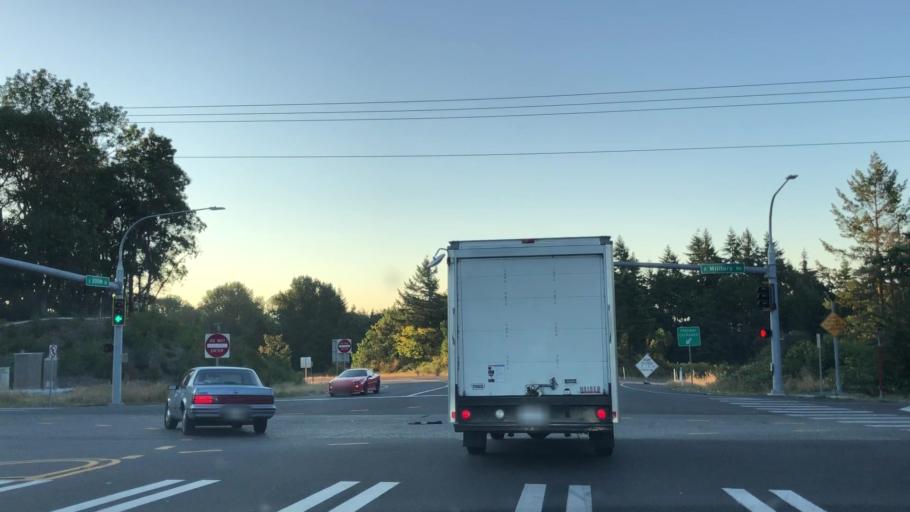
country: US
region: Washington
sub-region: King County
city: SeaTac
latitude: 47.4227
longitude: -122.2873
